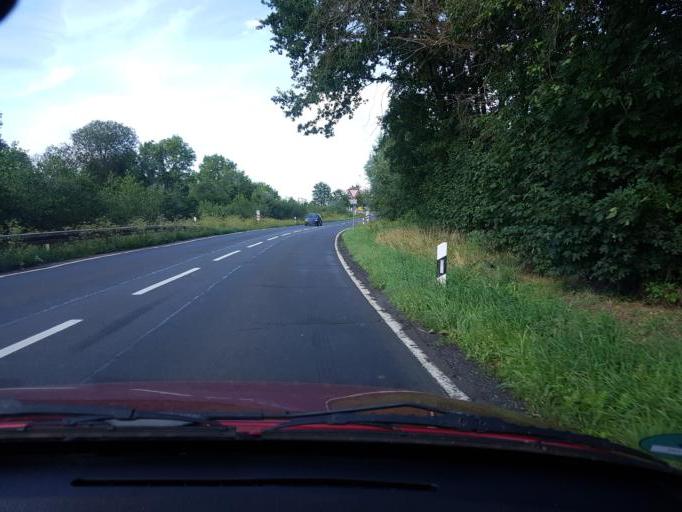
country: DE
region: Hesse
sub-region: Regierungsbezirk Giessen
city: Alten Buseck
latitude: 50.5905
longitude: 8.7311
